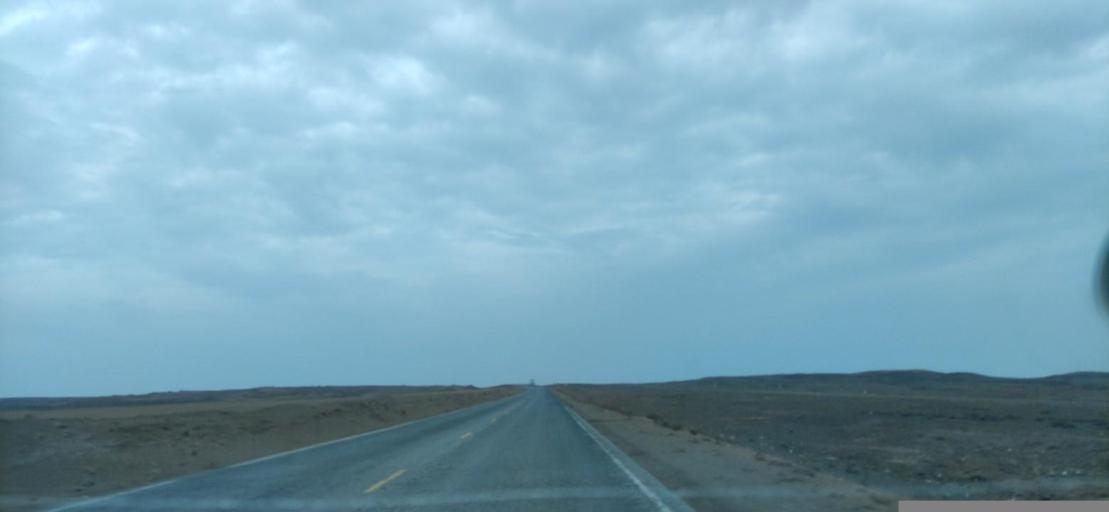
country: KZ
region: Qaraghandy
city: Saryshaghan
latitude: 46.3159
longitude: 73.7765
